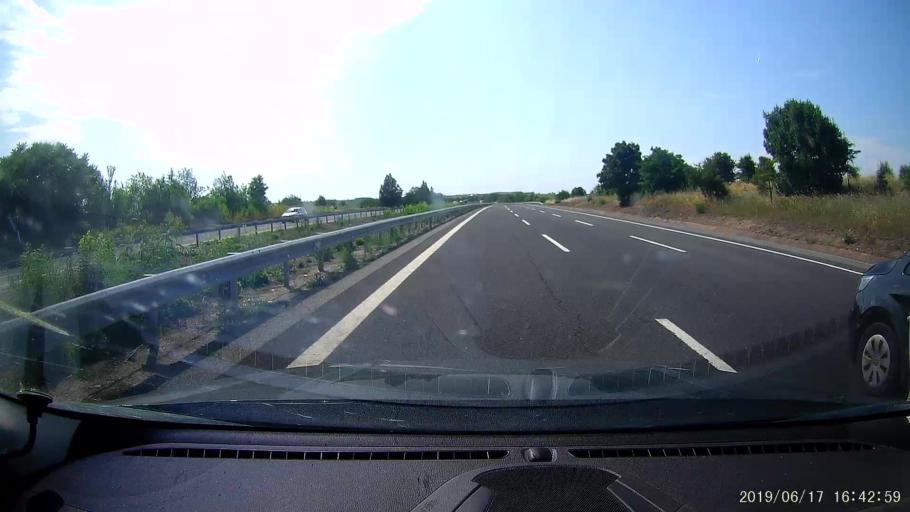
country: TR
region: Kirklareli
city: Luleburgaz
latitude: 41.4774
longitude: 27.3068
